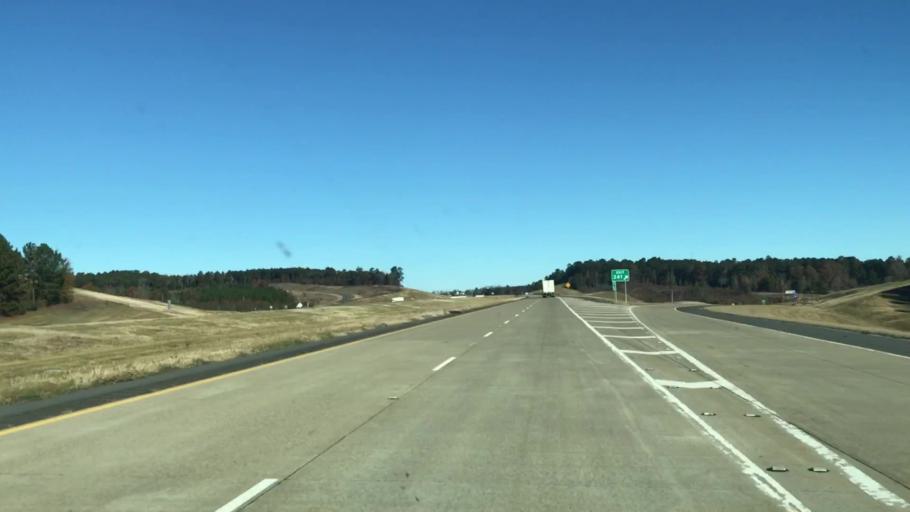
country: US
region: Louisiana
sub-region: Caddo Parish
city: Vivian
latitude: 32.9387
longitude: -93.8970
